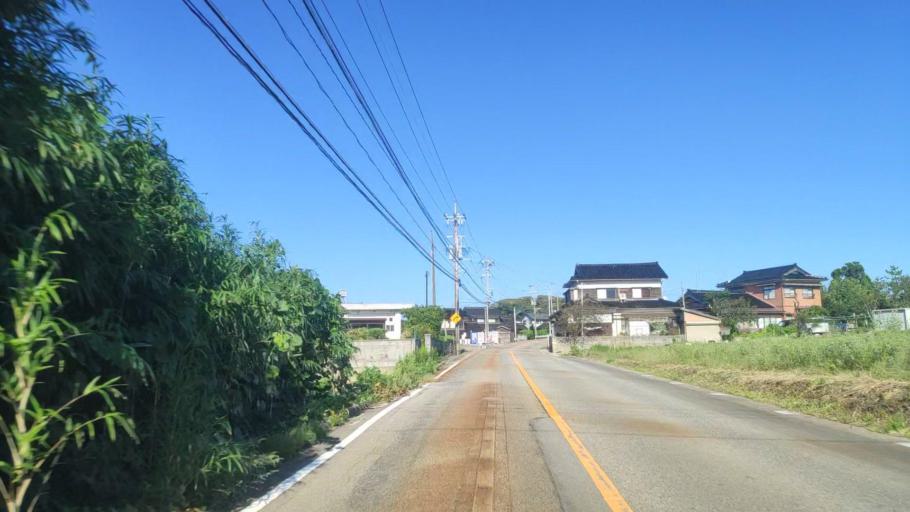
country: JP
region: Ishikawa
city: Hakui
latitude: 36.9256
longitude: 136.7614
